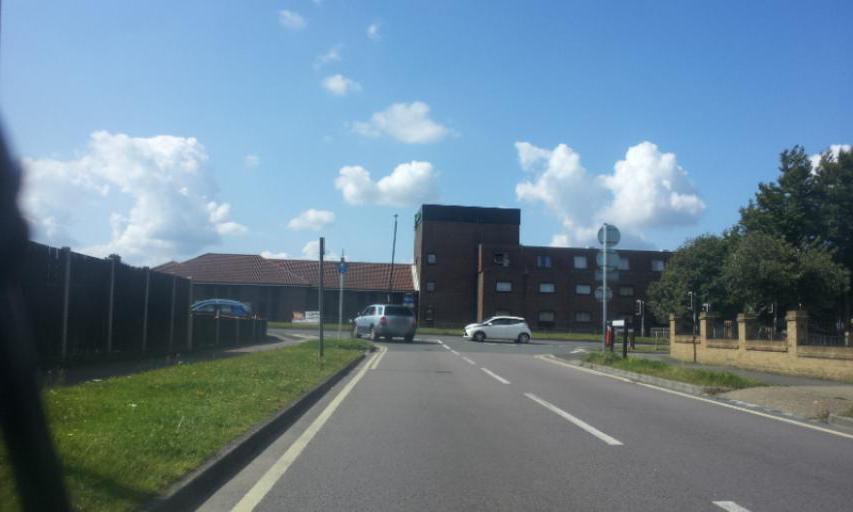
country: GB
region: England
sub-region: Kent
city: Chatham
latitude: 51.3490
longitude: 0.5089
